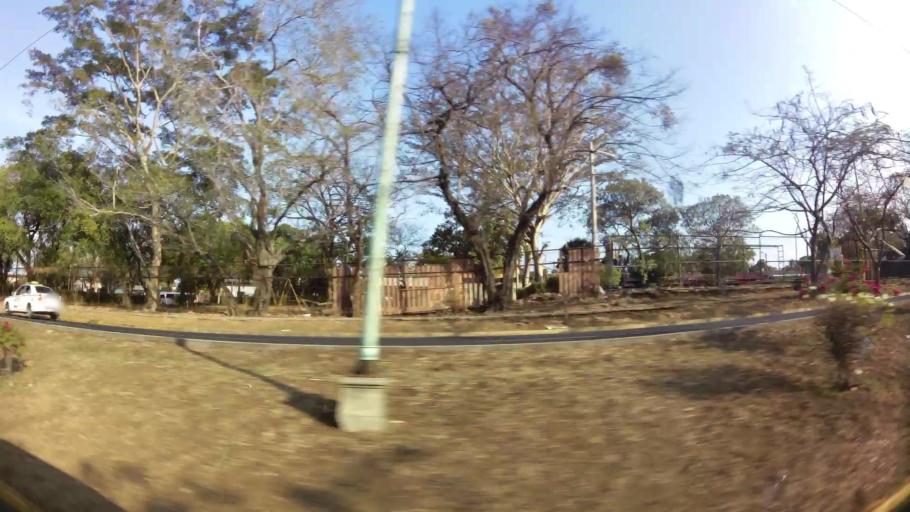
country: NI
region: Managua
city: Managua
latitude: 12.1210
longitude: -86.2713
